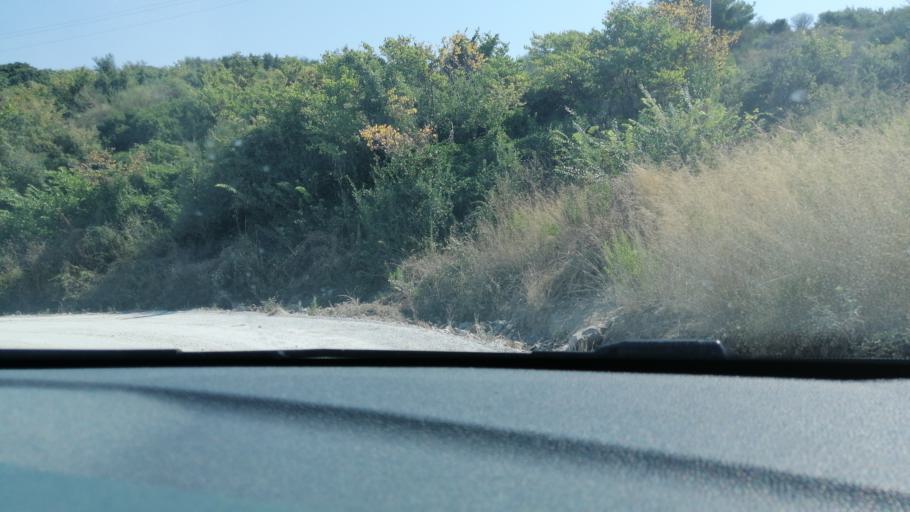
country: TR
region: Aydin
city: Davutlar
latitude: 37.7787
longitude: 27.3144
